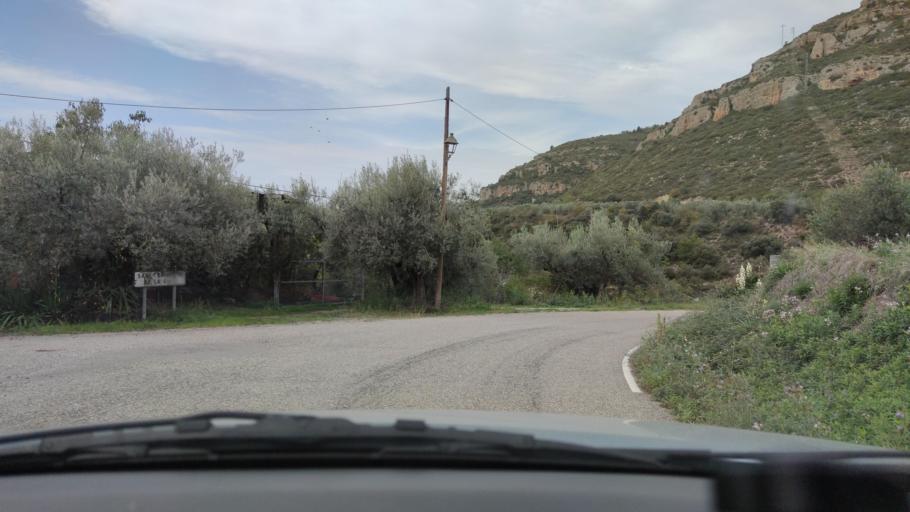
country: ES
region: Catalonia
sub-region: Provincia de Lleida
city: Llimiana
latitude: 42.0688
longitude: 0.9421
